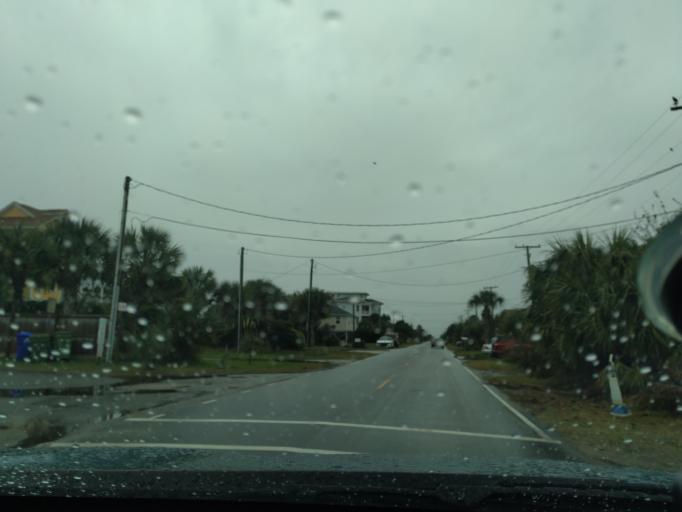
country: US
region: South Carolina
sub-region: Charleston County
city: Folly Beach
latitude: 32.6778
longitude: -79.8969
